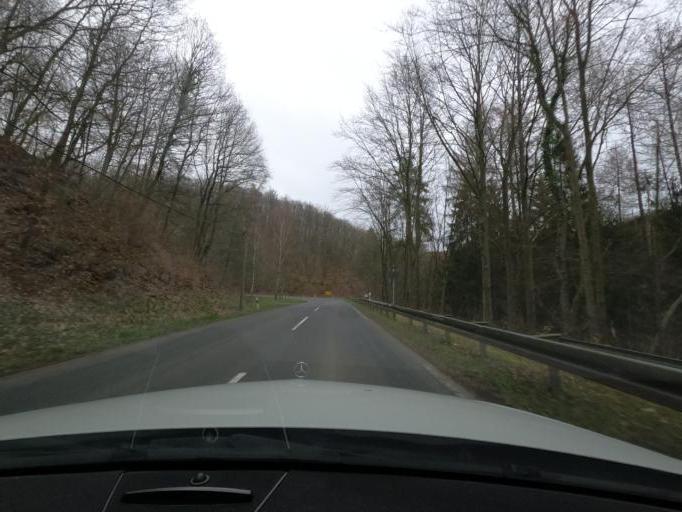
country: DE
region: Thuringia
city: Kella
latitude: 51.2148
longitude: 10.0671
